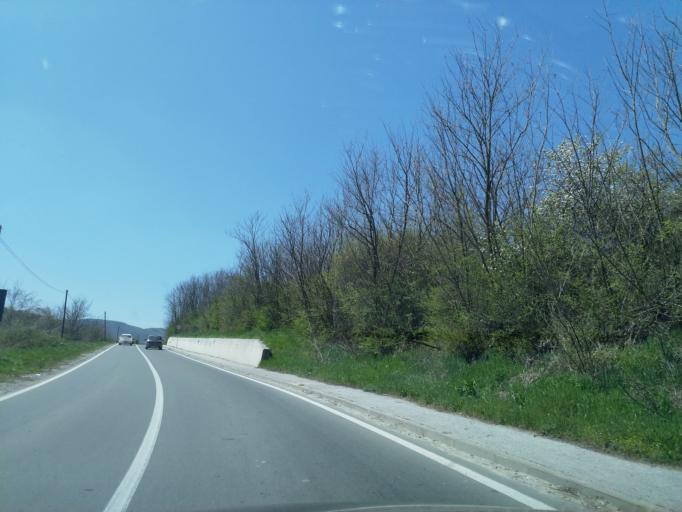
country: RS
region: Central Serbia
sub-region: Sumadijski Okrug
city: Arangelovac
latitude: 44.3355
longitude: 20.4938
